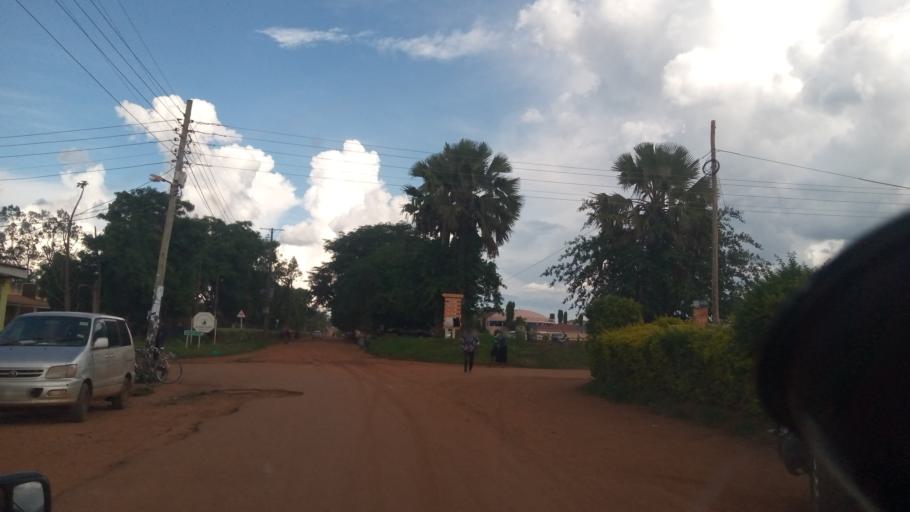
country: UG
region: Northern Region
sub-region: Lira District
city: Lira
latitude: 2.2410
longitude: 32.8963
